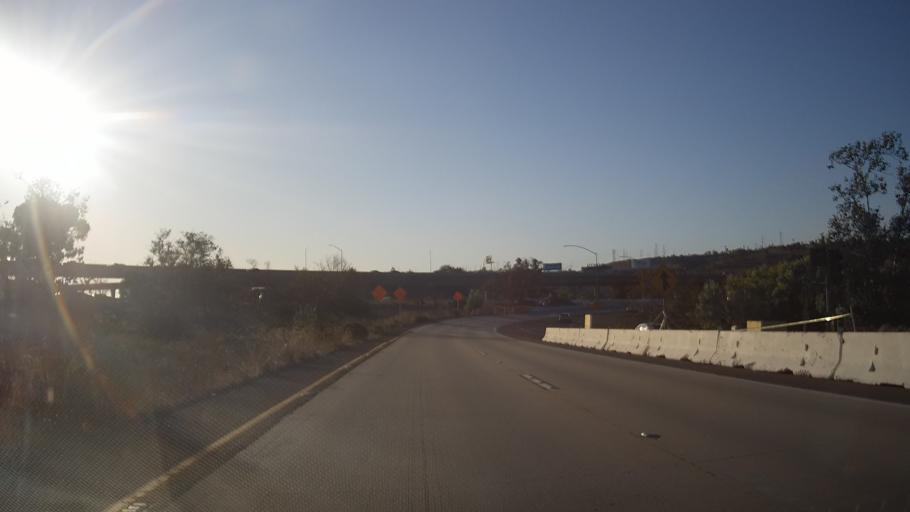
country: US
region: California
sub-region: San Diego County
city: San Diego
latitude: 32.7795
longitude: -117.1108
